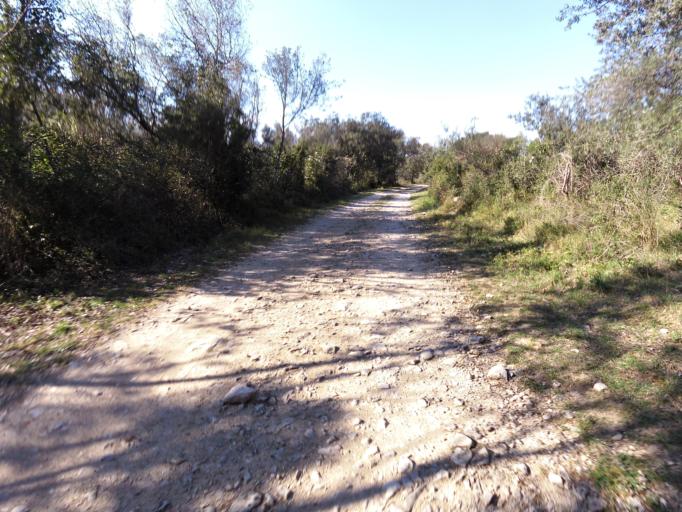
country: FR
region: Languedoc-Roussillon
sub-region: Departement du Gard
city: Congenies
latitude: 43.7537
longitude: 4.1689
